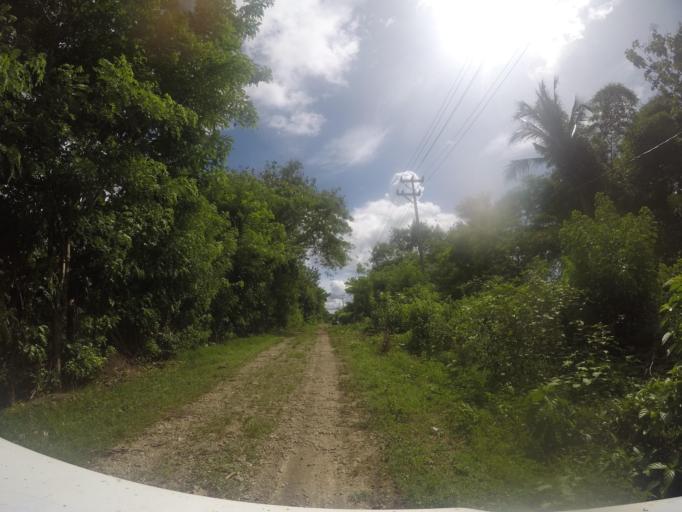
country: TL
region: Lautem
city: Lospalos
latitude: -8.4978
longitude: 127.0090
